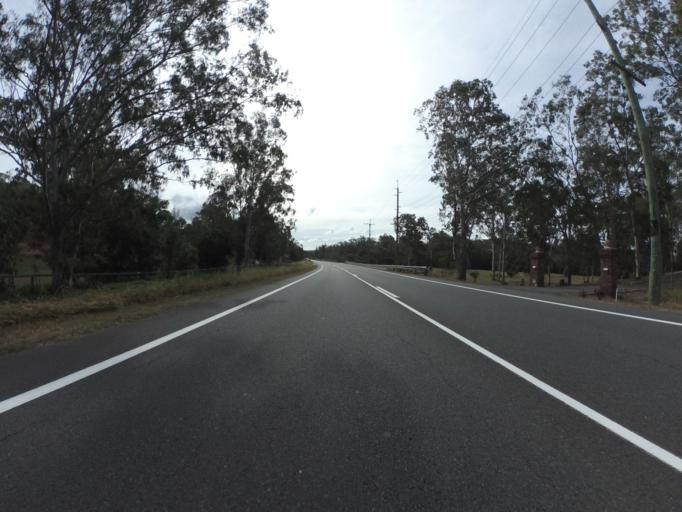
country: AU
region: Queensland
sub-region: Brisbane
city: Riverhills
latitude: -27.5517
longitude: 152.8890
